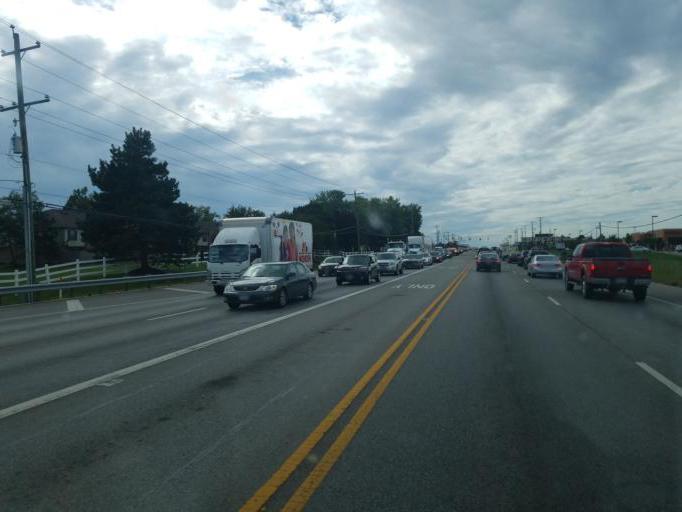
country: US
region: Ohio
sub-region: Franklin County
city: Reynoldsburg
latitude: 39.9817
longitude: -82.8240
